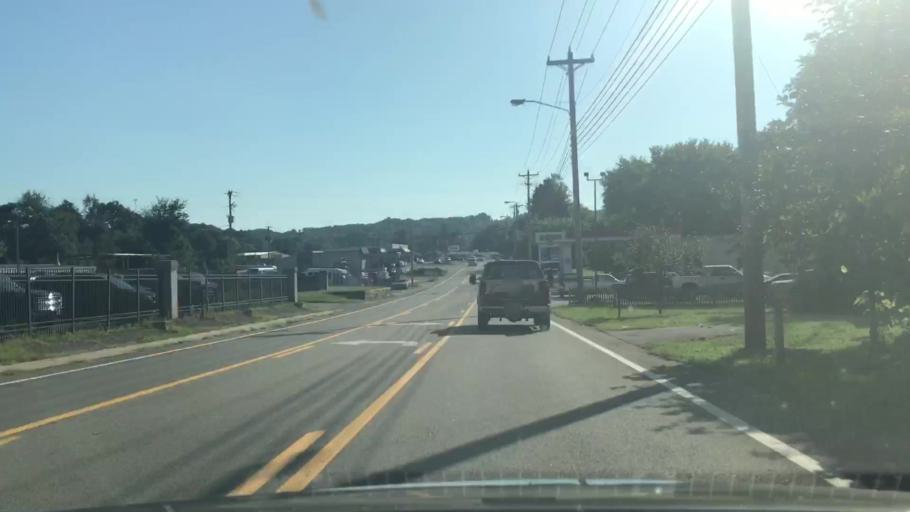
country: US
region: Tennessee
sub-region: Overton County
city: Livingston
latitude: 36.3879
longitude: -85.3088
